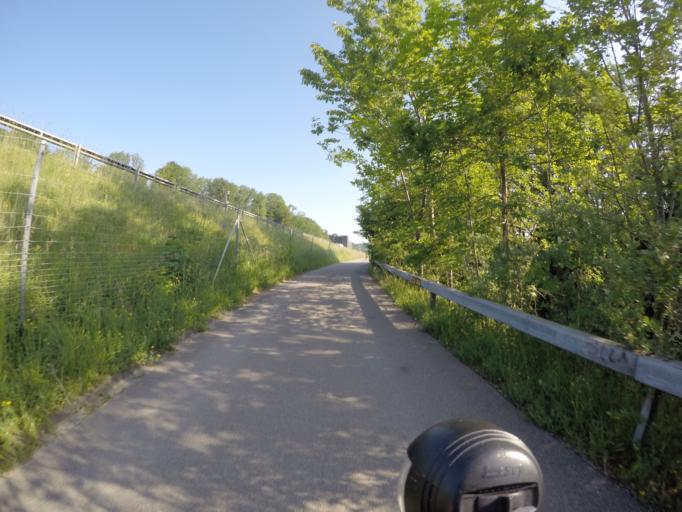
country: CH
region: Zurich
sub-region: Bezirk Winterthur
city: Toss
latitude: 47.4725
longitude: 8.7054
